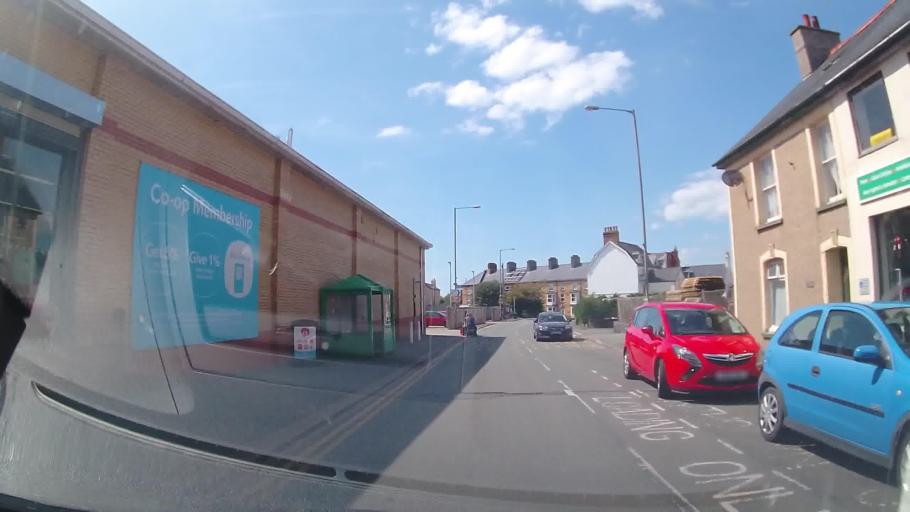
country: GB
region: Wales
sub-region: Gwynedd
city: Tywyn
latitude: 52.5849
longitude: -4.0920
